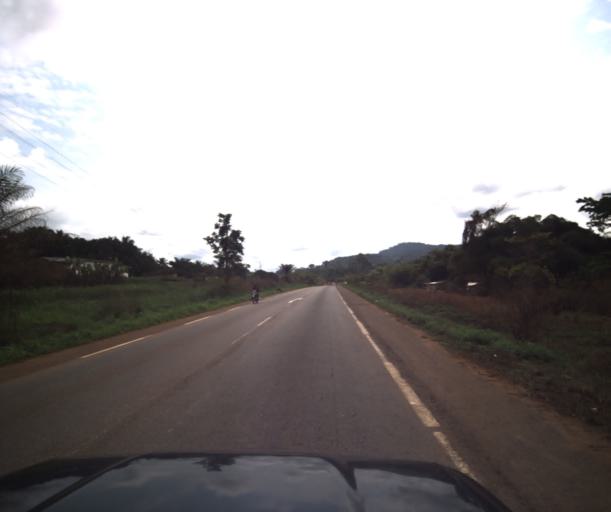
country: CM
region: Centre
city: Eseka
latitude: 3.8559
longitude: 10.5336
